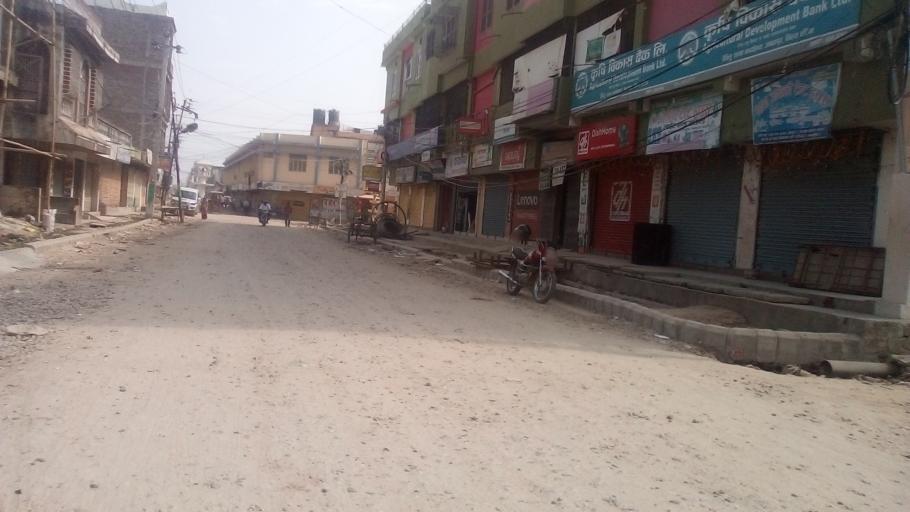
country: NP
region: Central Region
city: Janakpur
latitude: 26.7357
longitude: 85.9308
